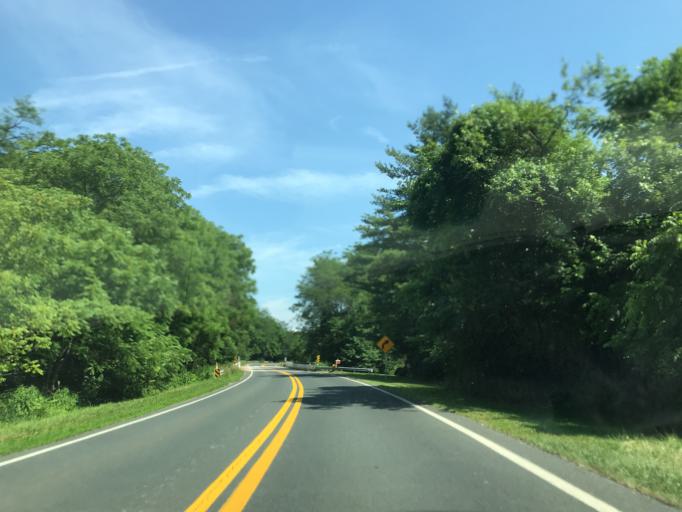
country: US
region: Maryland
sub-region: Carroll County
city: Taneytown
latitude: 39.6260
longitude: -77.1423
